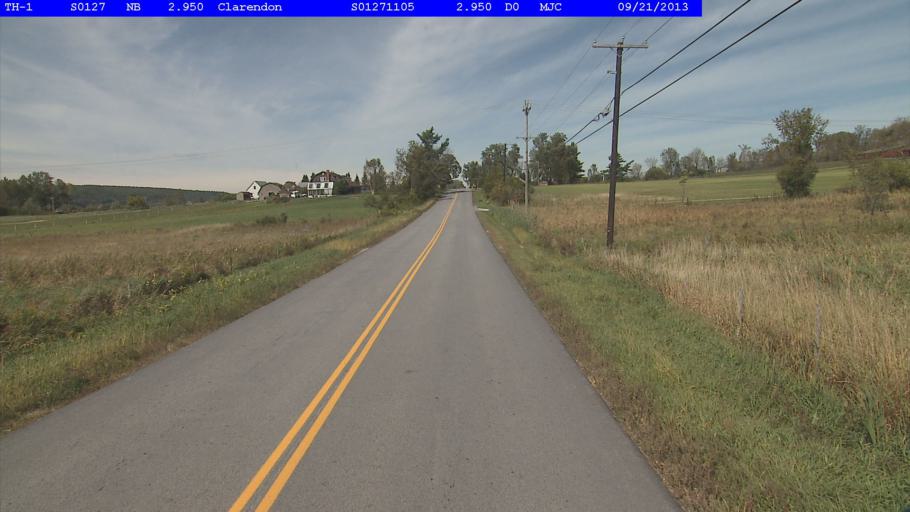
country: US
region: Vermont
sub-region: Rutland County
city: Rutland
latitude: 43.5558
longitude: -72.9712
